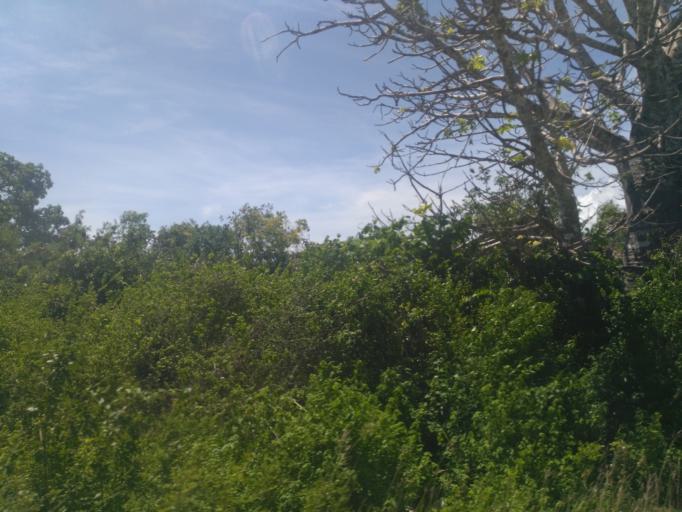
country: TZ
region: Zanzibar North
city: Gamba
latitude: -5.9258
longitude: 39.3508
